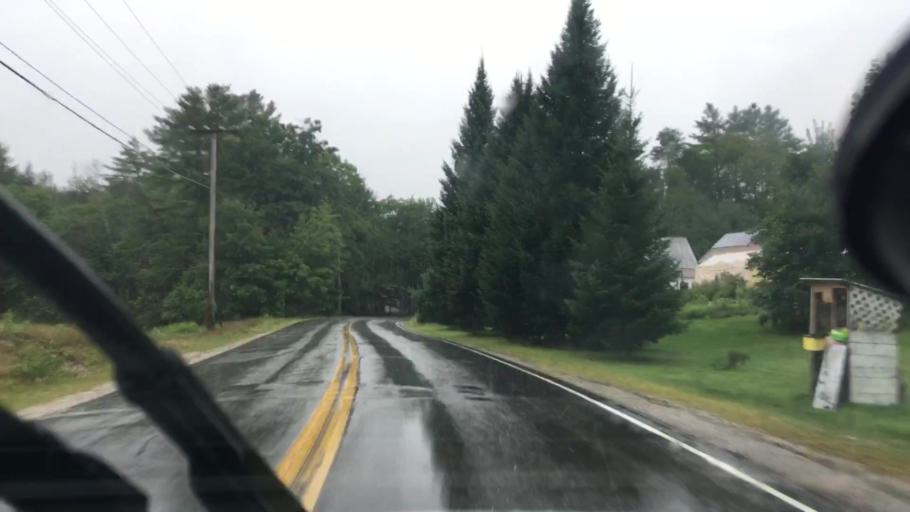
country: US
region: Maine
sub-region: Oxford County
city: Lovell
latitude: 44.2553
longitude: -70.8251
